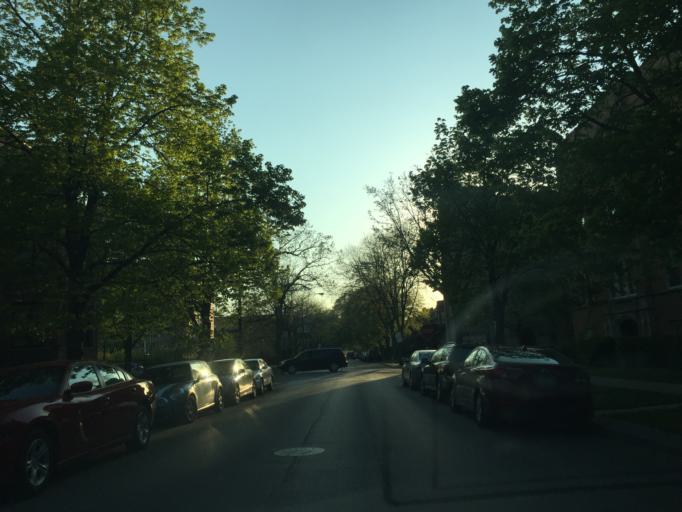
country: US
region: Illinois
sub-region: Cook County
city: Lincolnwood
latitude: 41.9649
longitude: -87.6905
